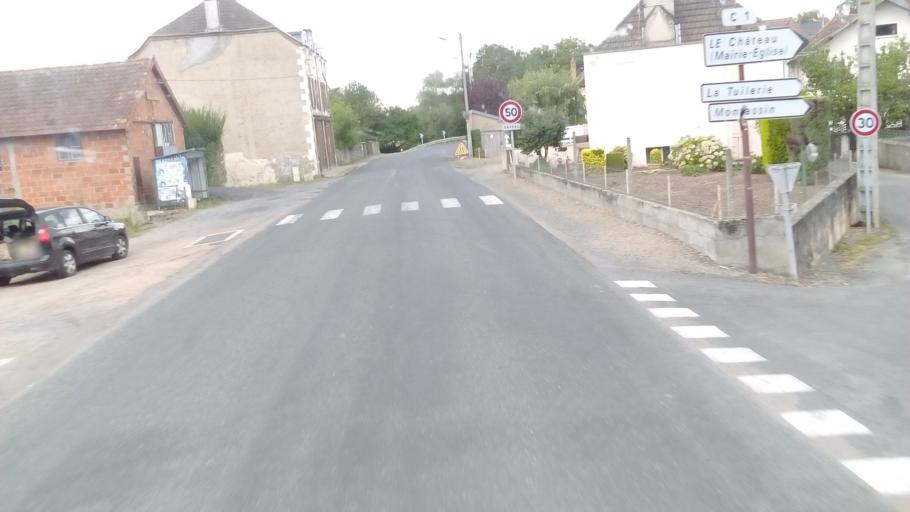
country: FR
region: Bourgogne
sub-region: Departement de Saone-et-Loire
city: La Motte-Saint-Jean
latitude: 46.4920
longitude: 3.9592
